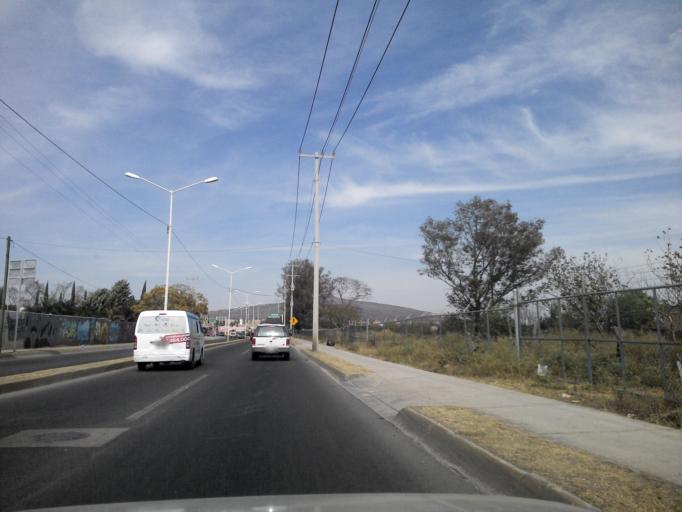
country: MX
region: Jalisco
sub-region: San Pedro Tlaquepaque
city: Paseo del Prado
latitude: 20.5609
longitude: -103.3933
